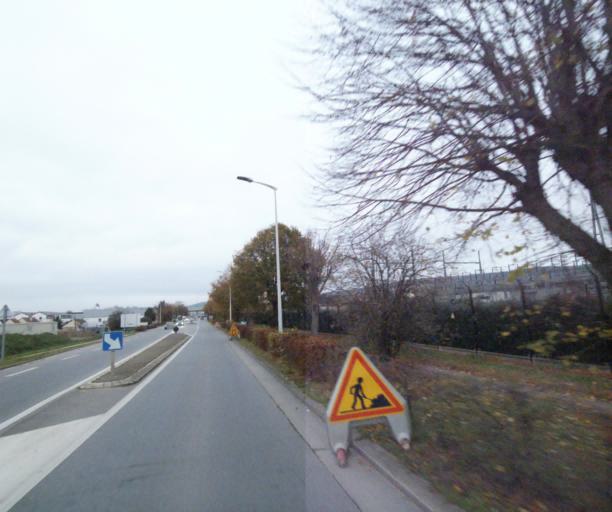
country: FR
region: Ile-de-France
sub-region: Departement des Yvelines
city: Triel-sur-Seine
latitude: 48.9660
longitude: 2.0124
